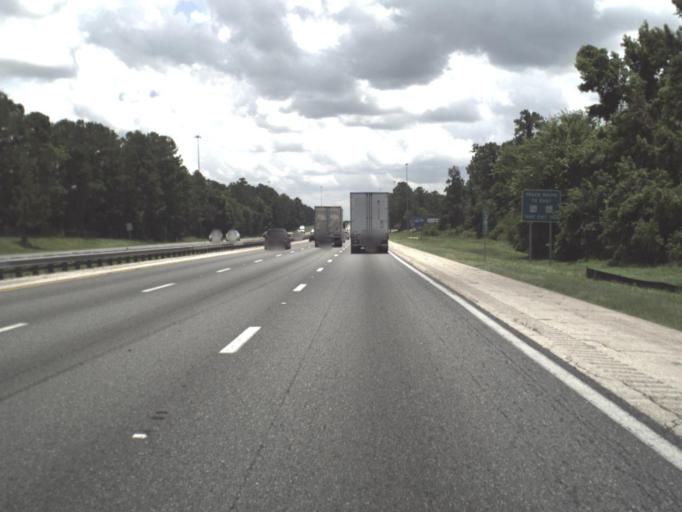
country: US
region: Florida
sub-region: Alachua County
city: Gainesville
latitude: 29.6083
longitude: -82.3791
